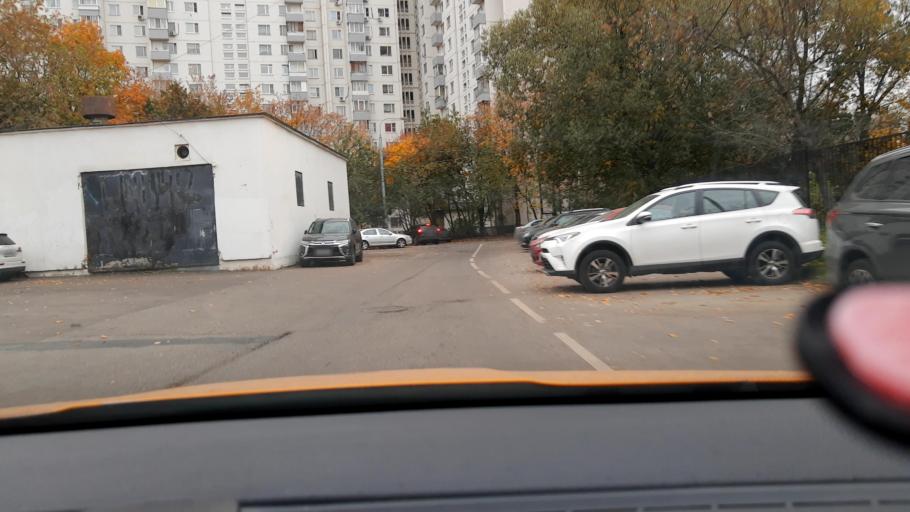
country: RU
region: Moskovskaya
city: Bol'shaya Setun'
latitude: 55.7239
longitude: 37.4418
